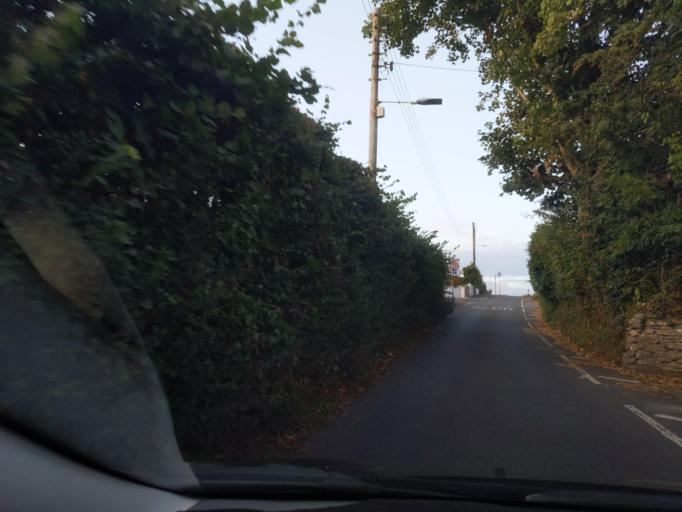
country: GB
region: England
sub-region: Plymouth
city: Plymstock
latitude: 50.3591
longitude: -4.0719
